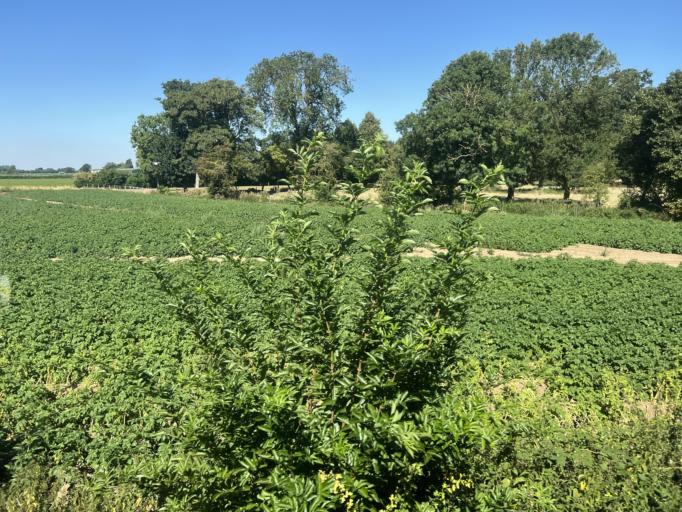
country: GB
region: England
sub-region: Lincolnshire
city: Boston
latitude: 52.9956
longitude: -0.0242
